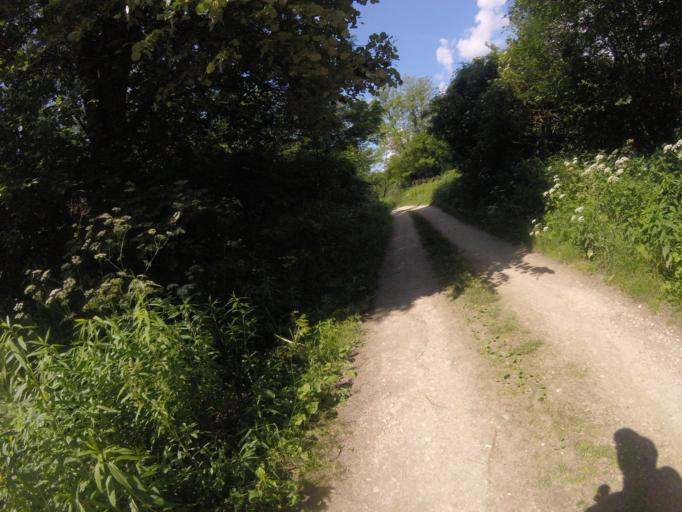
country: HU
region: Veszprem
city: Cseteny
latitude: 47.2807
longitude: 18.0222
